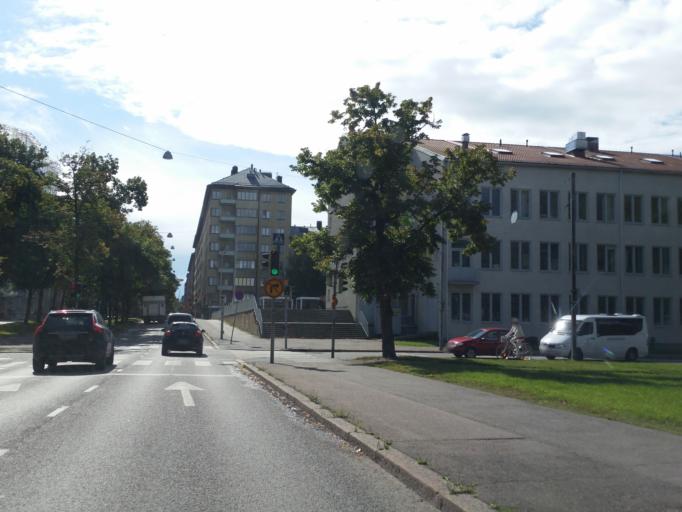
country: FI
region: Uusimaa
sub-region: Helsinki
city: Helsinki
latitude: 60.1762
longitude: 24.9177
